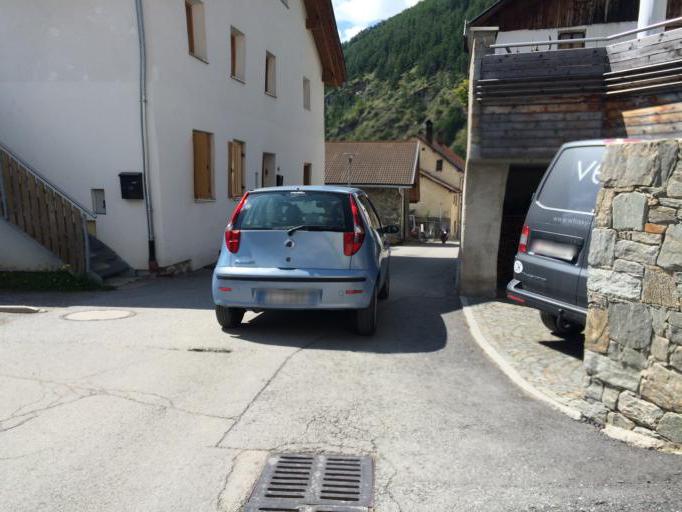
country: IT
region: Trentino-Alto Adige
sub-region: Bolzano
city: Malles Venosta
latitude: 46.6940
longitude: 10.5217
